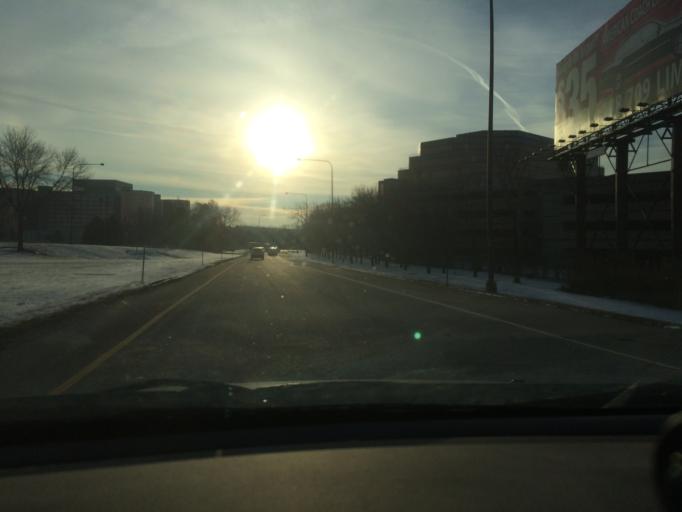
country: US
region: Illinois
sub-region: Cook County
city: Rosemont
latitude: 41.9827
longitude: -87.8644
